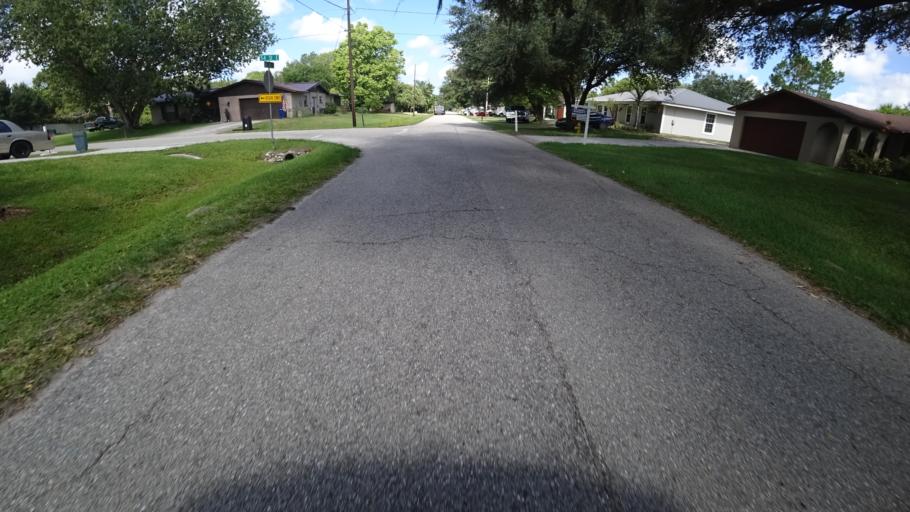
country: US
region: Florida
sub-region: Manatee County
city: Samoset
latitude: 27.4833
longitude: -82.4934
